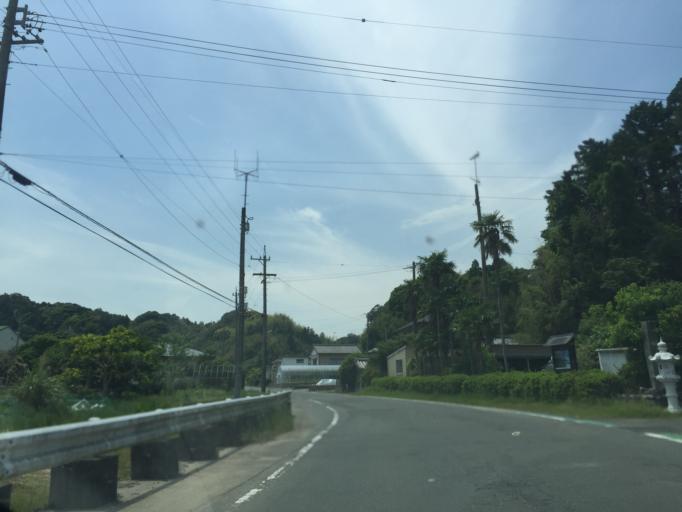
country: JP
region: Shizuoka
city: Kakegawa
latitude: 34.7952
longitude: 137.9751
